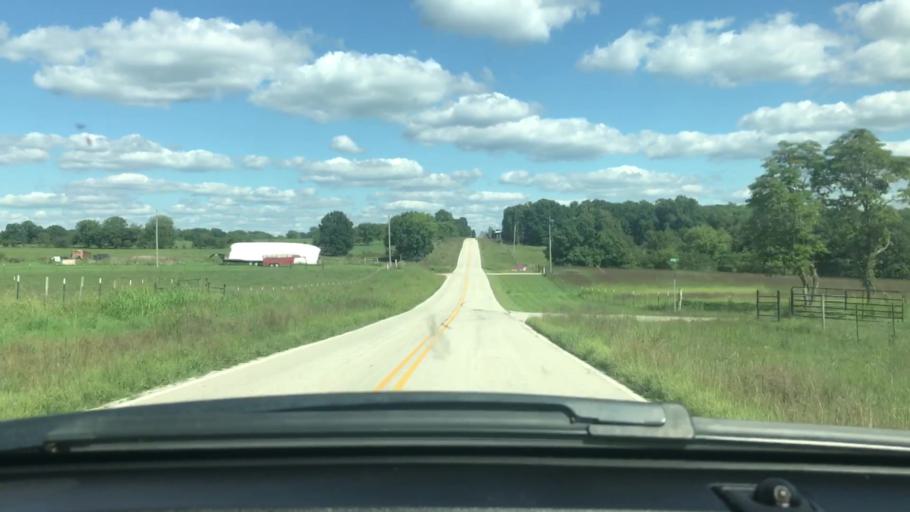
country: US
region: Missouri
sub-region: Wright County
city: Hartville
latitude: 37.3770
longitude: -92.4155
